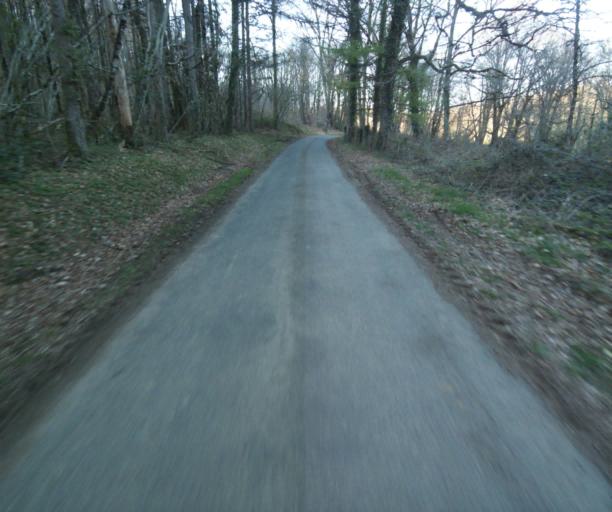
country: FR
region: Limousin
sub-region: Departement de la Correze
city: Seilhac
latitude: 45.3483
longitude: 1.7201
